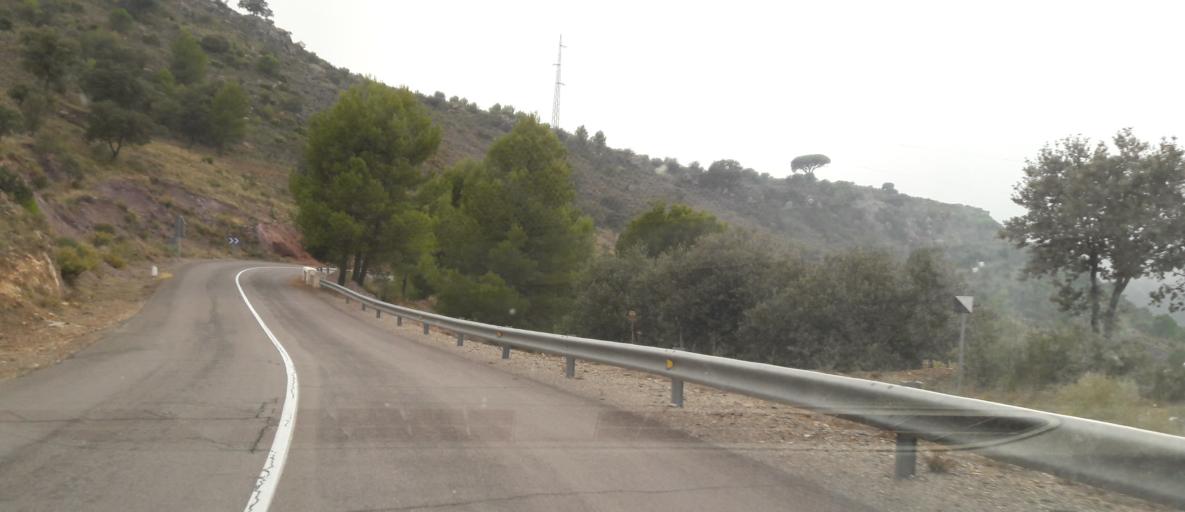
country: ES
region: Andalusia
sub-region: Provincia de Almeria
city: Enix
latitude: 36.8938
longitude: -2.6130
